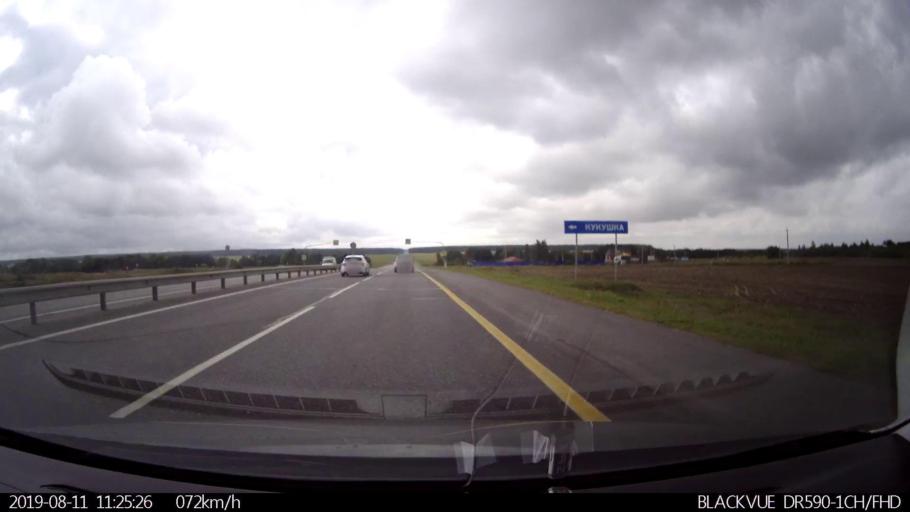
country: RU
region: Ulyanovsk
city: Krasnyy Gulyay
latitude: 54.1172
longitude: 48.2382
